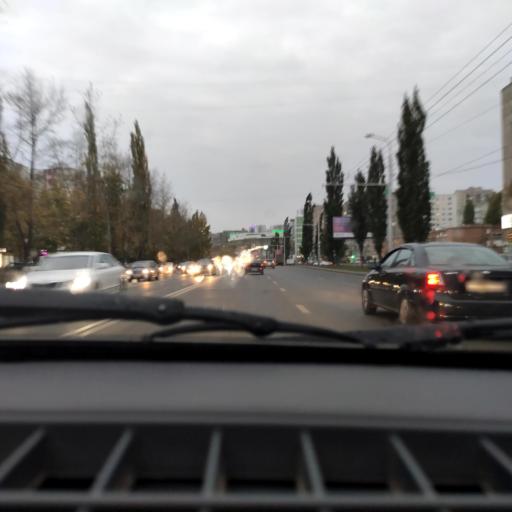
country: RU
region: Bashkortostan
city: Ufa
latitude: 54.7686
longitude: 56.0549
